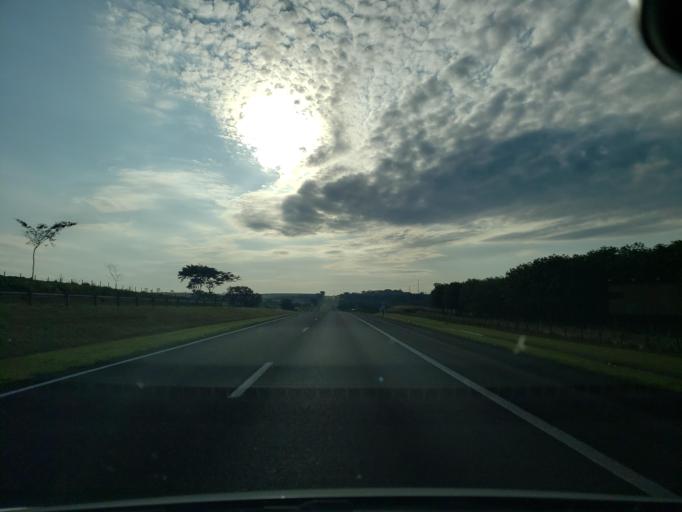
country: BR
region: Sao Paulo
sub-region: Valparaiso
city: Valparaiso
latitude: -21.1704
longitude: -50.9337
